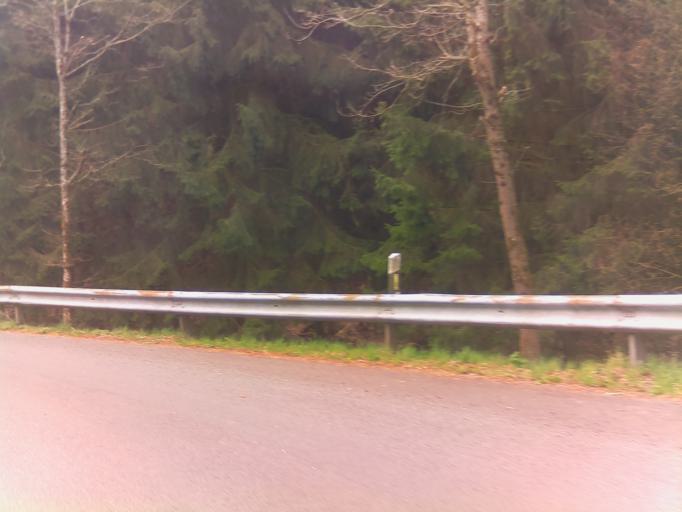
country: DE
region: Rheinland-Pfalz
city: Siesbach
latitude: 49.7373
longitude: 7.2396
